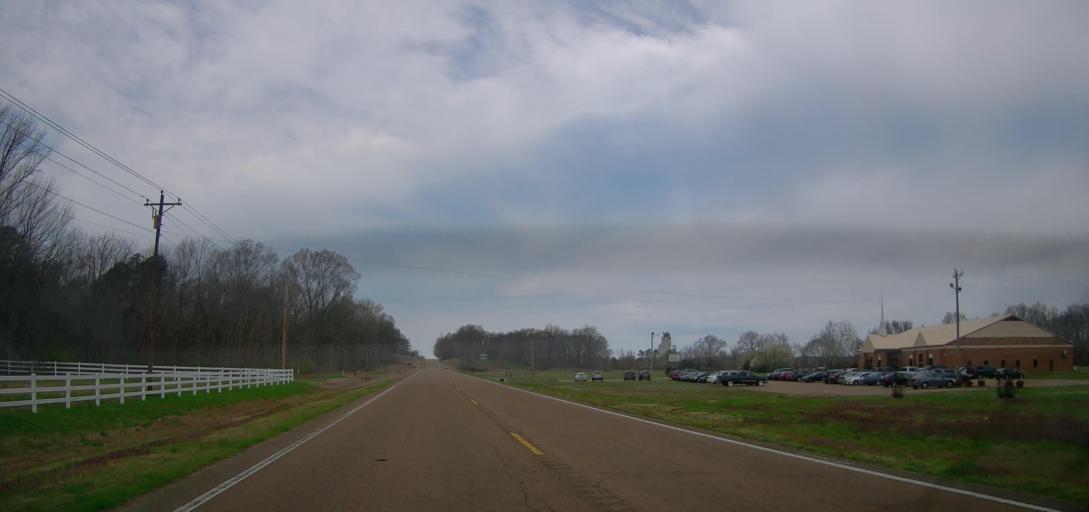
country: US
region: Mississippi
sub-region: Marshall County
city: Byhalia
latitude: 34.8569
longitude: -89.6459
